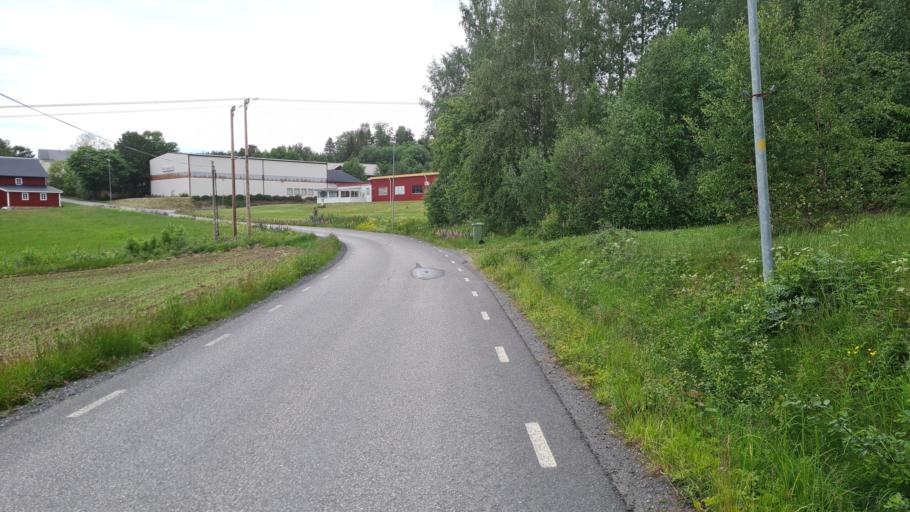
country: SE
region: Vaesternorrland
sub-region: Kramfors Kommun
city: Nordingra
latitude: 62.9814
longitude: 18.4317
